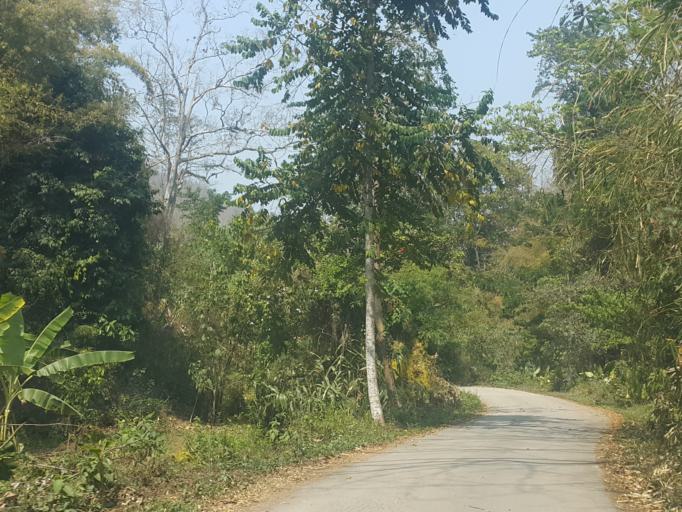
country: TH
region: Chiang Mai
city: Hang Dong
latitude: 18.7319
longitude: 98.8292
